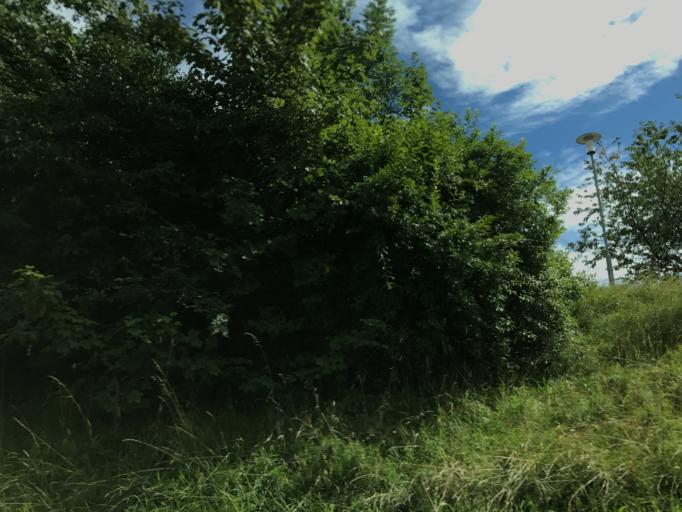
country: DE
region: Baden-Wuerttemberg
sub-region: Tuebingen Region
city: Wangen im Allgau
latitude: 47.6832
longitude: 9.8418
